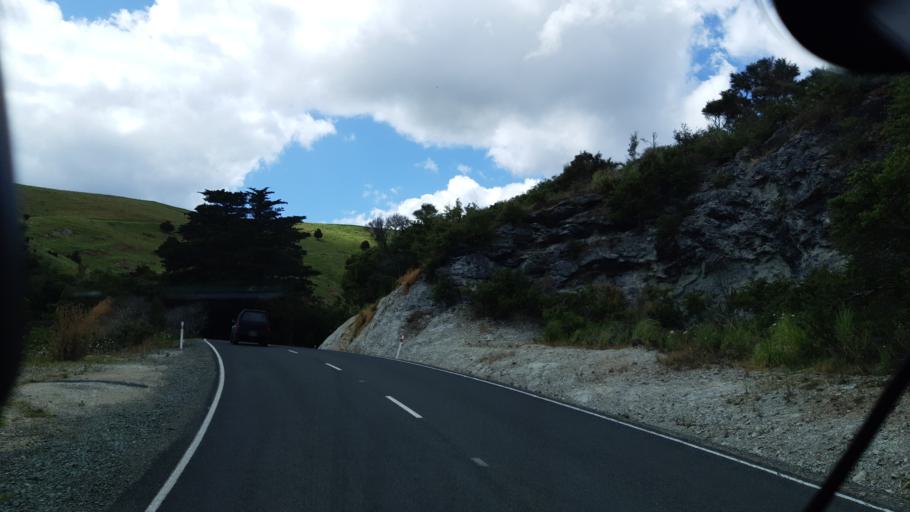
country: NZ
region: Northland
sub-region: Far North District
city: Taipa
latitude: -35.2440
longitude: 173.5345
